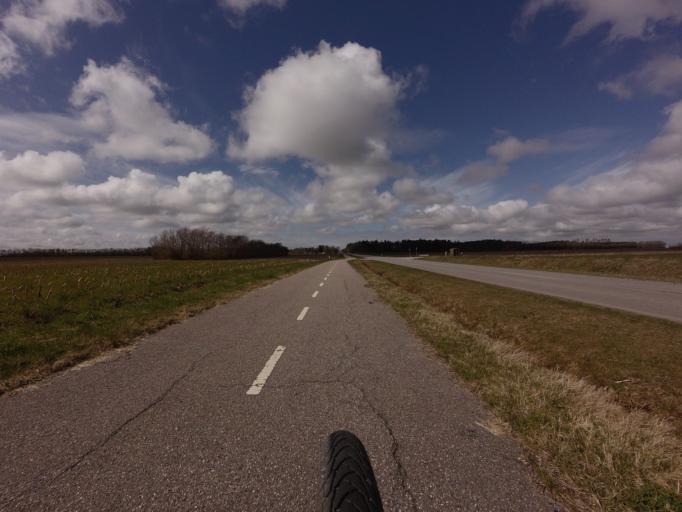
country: DK
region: North Denmark
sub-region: Hjorring Kommune
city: Vra
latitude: 57.3550
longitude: 9.8914
